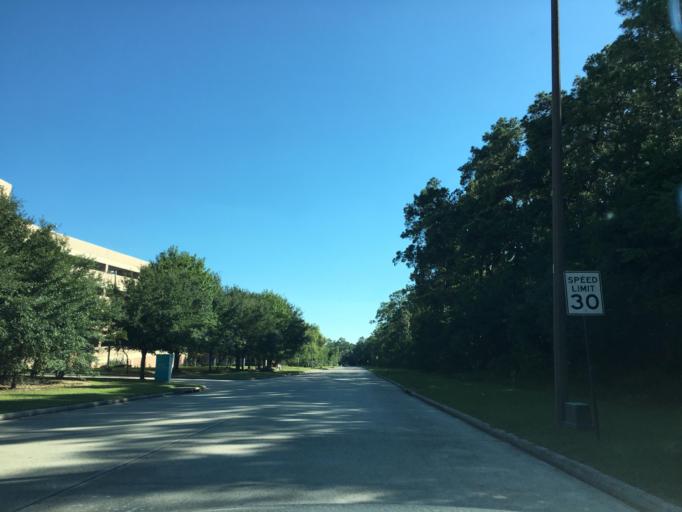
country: US
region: Texas
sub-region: Montgomery County
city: Shenandoah
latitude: 30.2044
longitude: -95.4596
